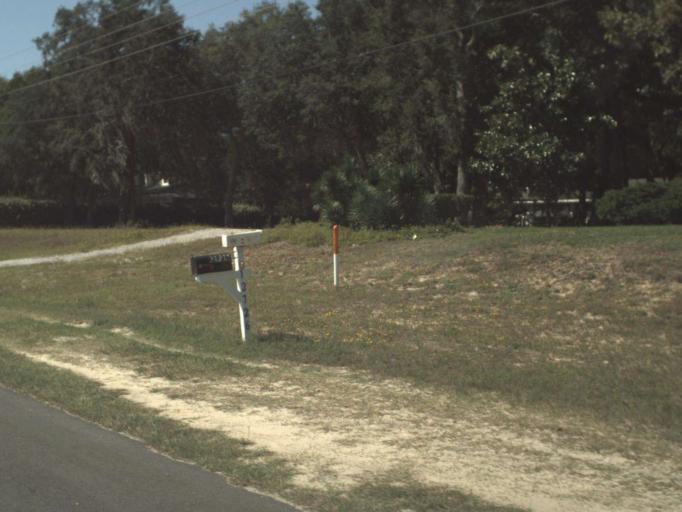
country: US
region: Florida
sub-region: Walton County
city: Miramar Beach
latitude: 30.4752
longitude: -86.3346
